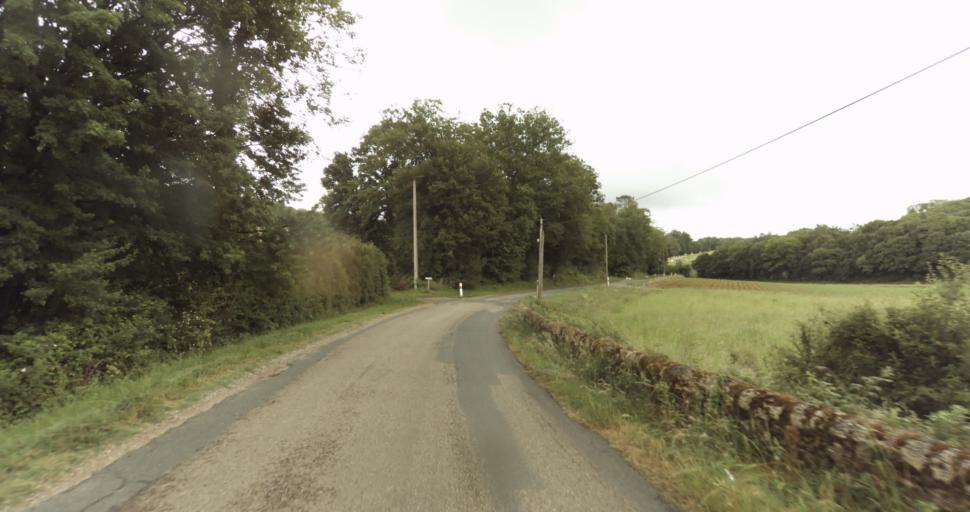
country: FR
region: Aquitaine
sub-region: Departement de la Dordogne
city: Belves
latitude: 44.7552
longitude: 0.9271
